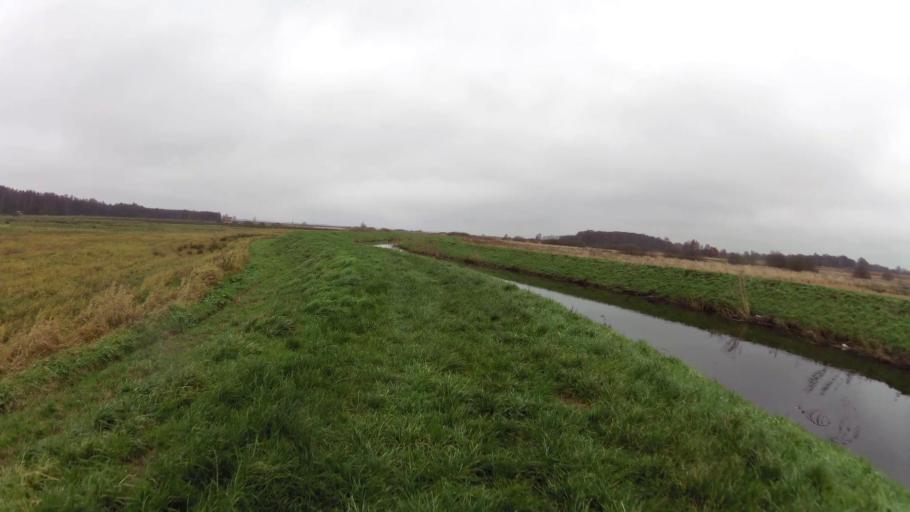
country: PL
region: West Pomeranian Voivodeship
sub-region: Koszalin
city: Koszalin
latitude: 54.2434
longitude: 16.1290
